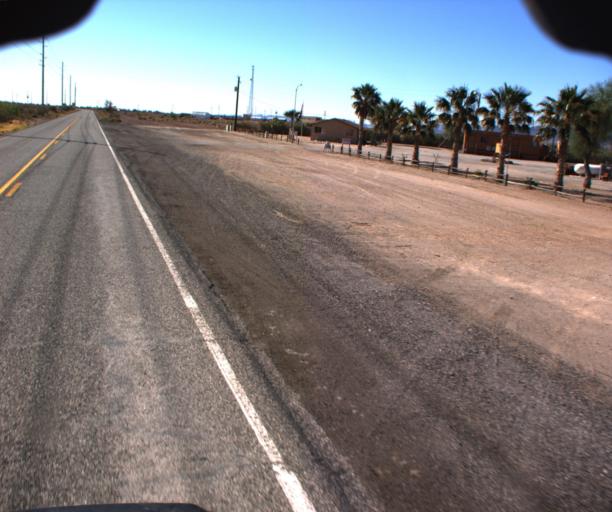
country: US
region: Arizona
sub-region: La Paz County
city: Quartzsite
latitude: 33.9181
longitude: -113.9947
